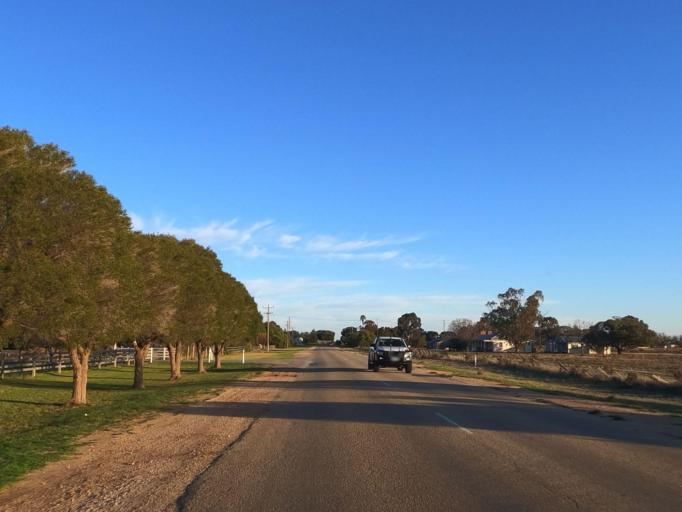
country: AU
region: Victoria
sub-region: Swan Hill
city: Swan Hill
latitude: -35.3576
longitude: 143.5522
